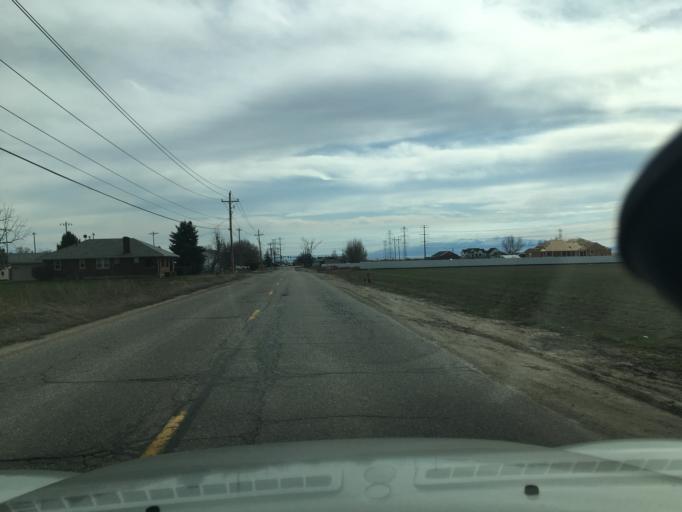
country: US
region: Utah
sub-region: Davis County
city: Layton
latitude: 41.0638
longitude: -112.0071
